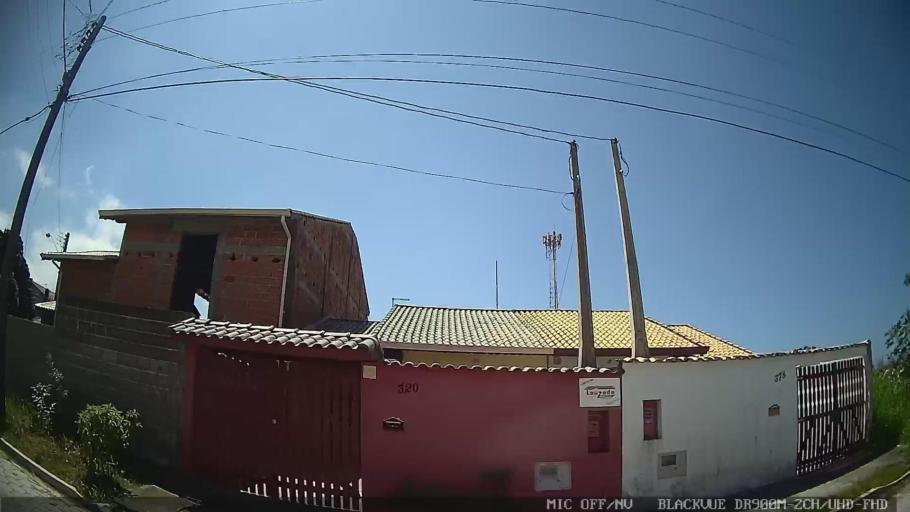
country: BR
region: Sao Paulo
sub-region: Peruibe
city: Peruibe
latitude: -24.3015
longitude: -46.9940
